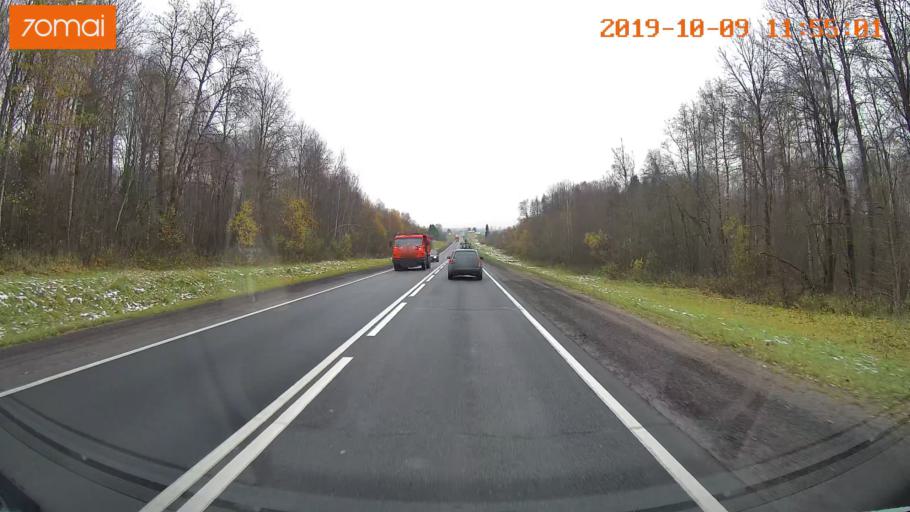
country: RU
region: Vologda
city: Gryazovets
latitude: 58.7523
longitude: 40.2842
